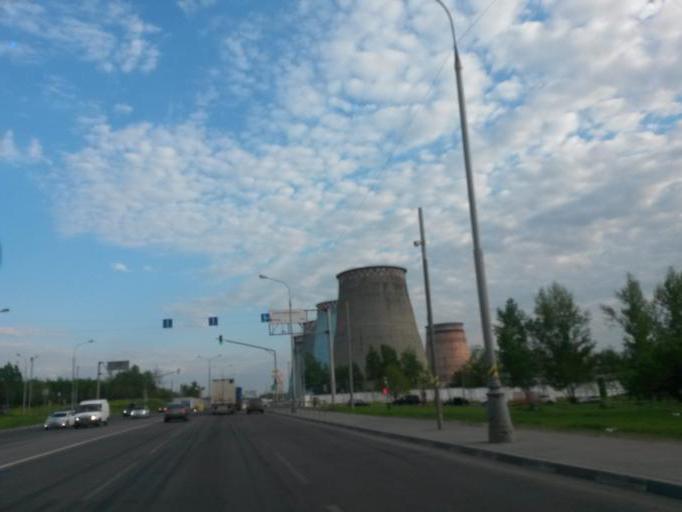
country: RU
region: Moskovskaya
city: Biryulevo Zapadnoye
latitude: 55.5818
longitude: 37.6378
